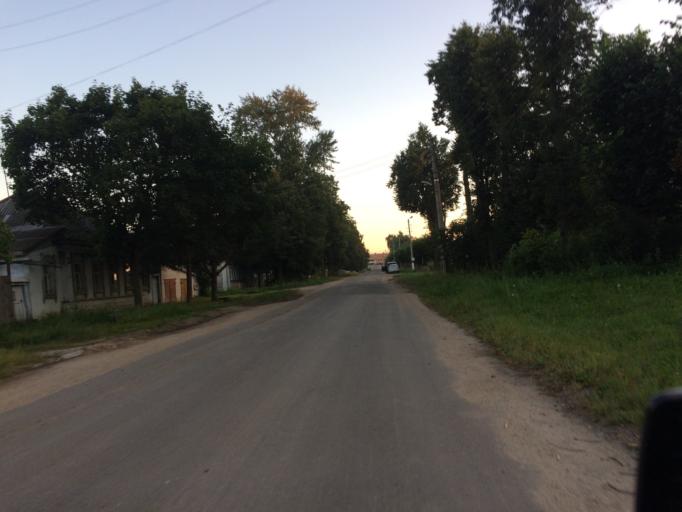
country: RU
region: Mariy-El
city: Yoshkar-Ola
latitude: 56.6410
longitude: 47.9103
